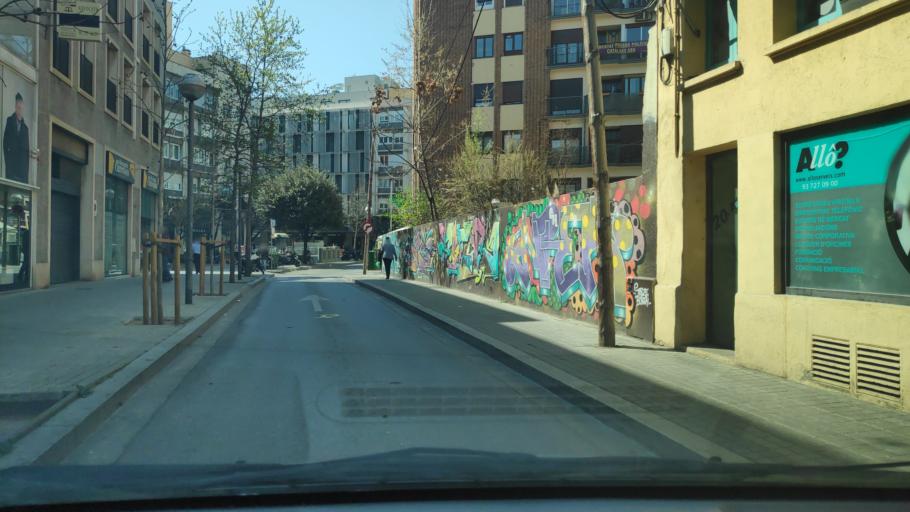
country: ES
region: Catalonia
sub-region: Provincia de Barcelona
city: Sabadell
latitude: 41.5495
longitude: 2.1090
